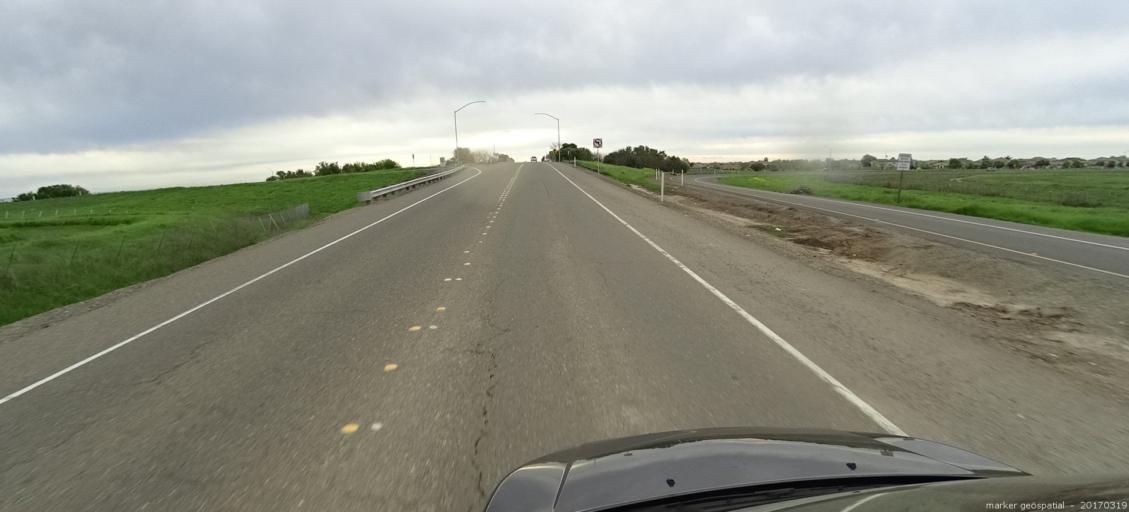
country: US
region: California
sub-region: Sacramento County
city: Elverta
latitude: 38.6855
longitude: -121.5432
